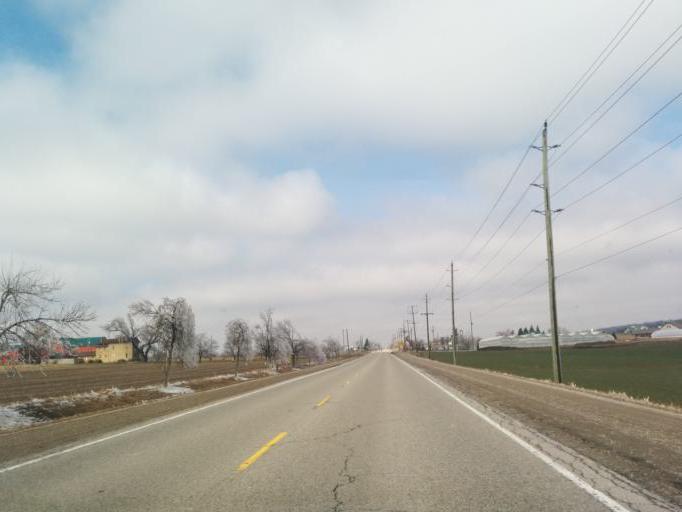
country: CA
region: Ontario
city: Waterloo
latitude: 43.6285
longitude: -80.5508
